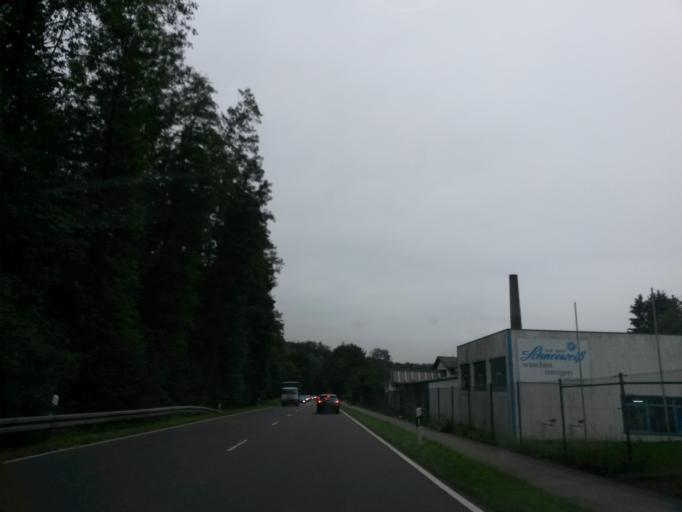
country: DE
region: North Rhine-Westphalia
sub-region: Regierungsbezirk Koln
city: Gummersbach
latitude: 51.0179
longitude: 7.5565
